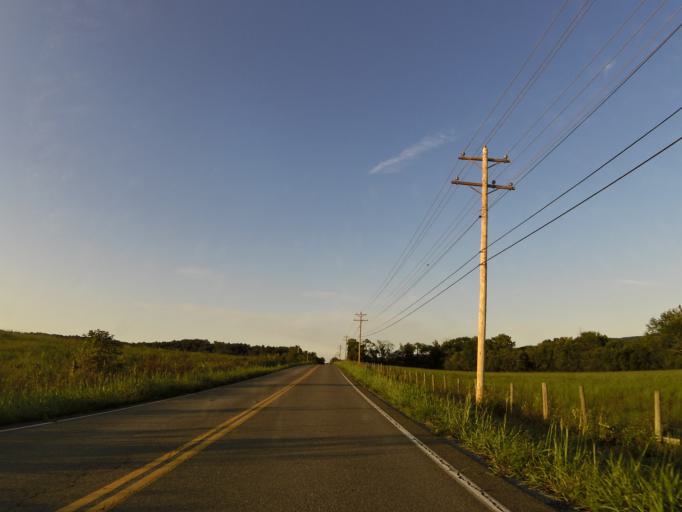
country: US
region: Tennessee
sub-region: Roane County
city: Rockwood
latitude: 35.7002
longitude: -84.6526
